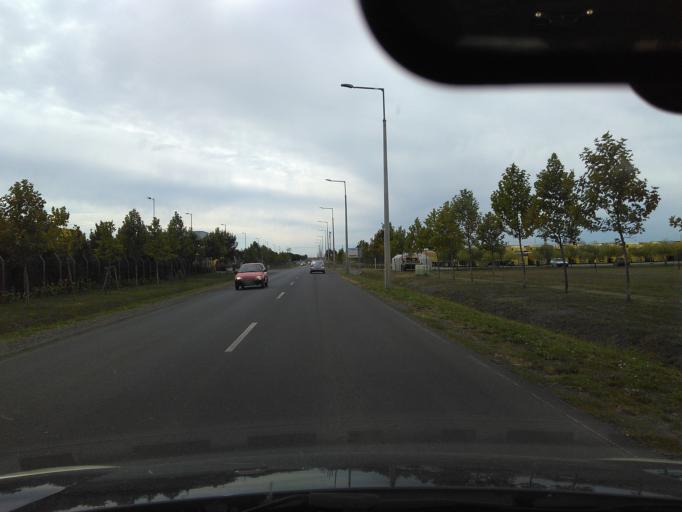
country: HU
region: Heves
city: Hatvan
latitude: 47.6750
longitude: 19.6527
